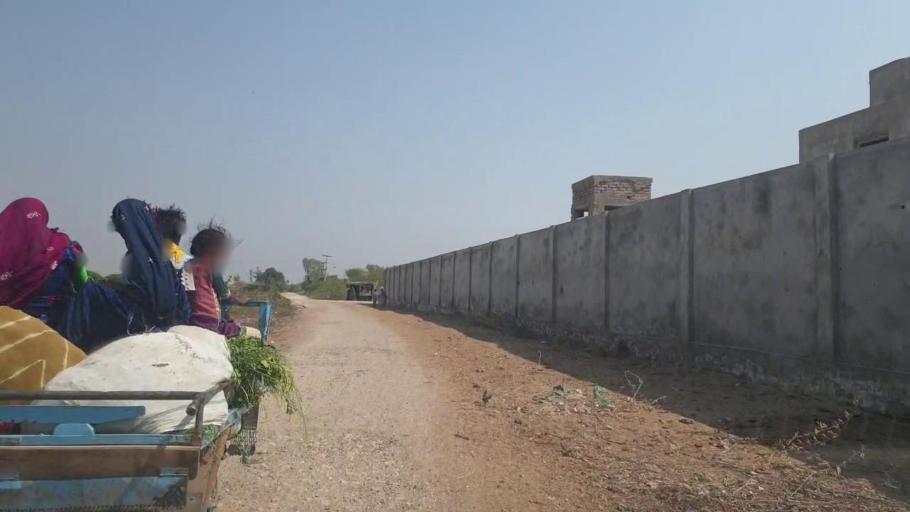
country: PK
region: Sindh
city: Dhoro Naro
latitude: 25.4876
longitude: 69.5640
